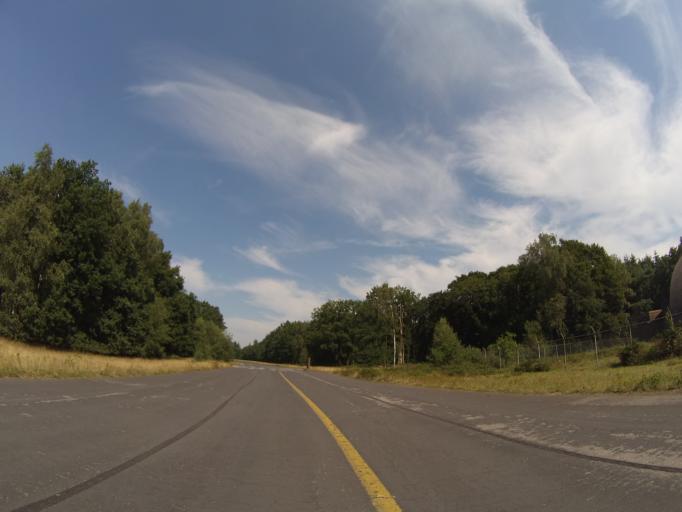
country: NL
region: Utrecht
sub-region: Gemeente Zeist
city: Zeist
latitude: 52.1308
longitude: 5.2589
